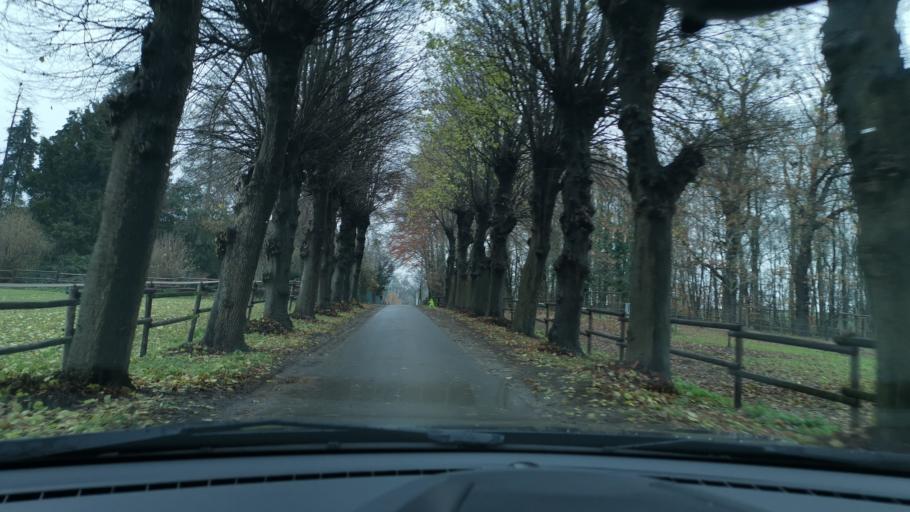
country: DE
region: North Rhine-Westphalia
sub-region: Regierungsbezirk Dusseldorf
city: Juchen
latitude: 51.1116
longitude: 6.5230
